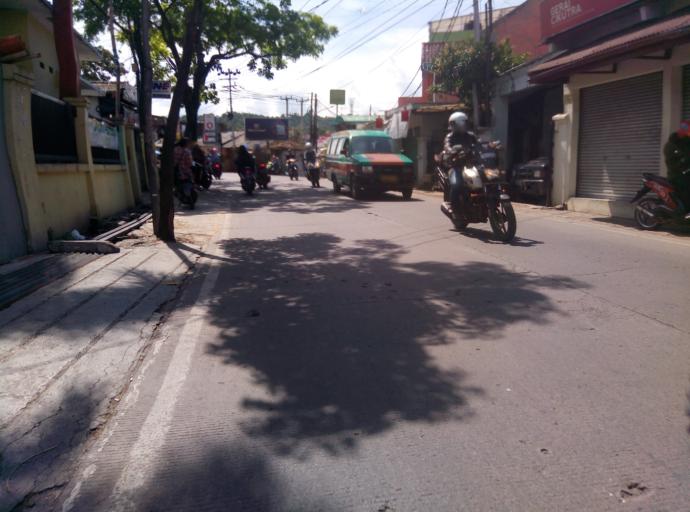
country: ID
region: West Java
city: Bandung
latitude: -6.8963
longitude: 107.6436
